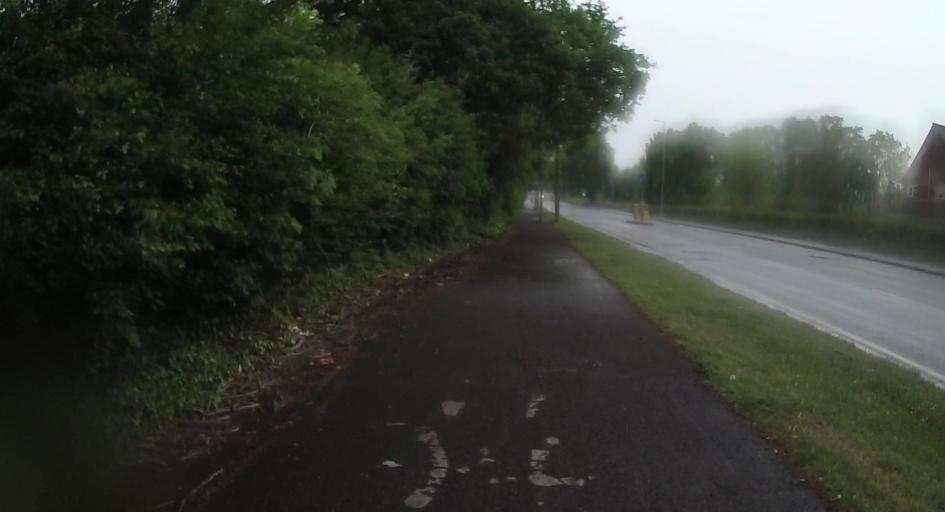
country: GB
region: England
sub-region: Bracknell Forest
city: Bracknell
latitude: 51.4182
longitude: -0.7622
